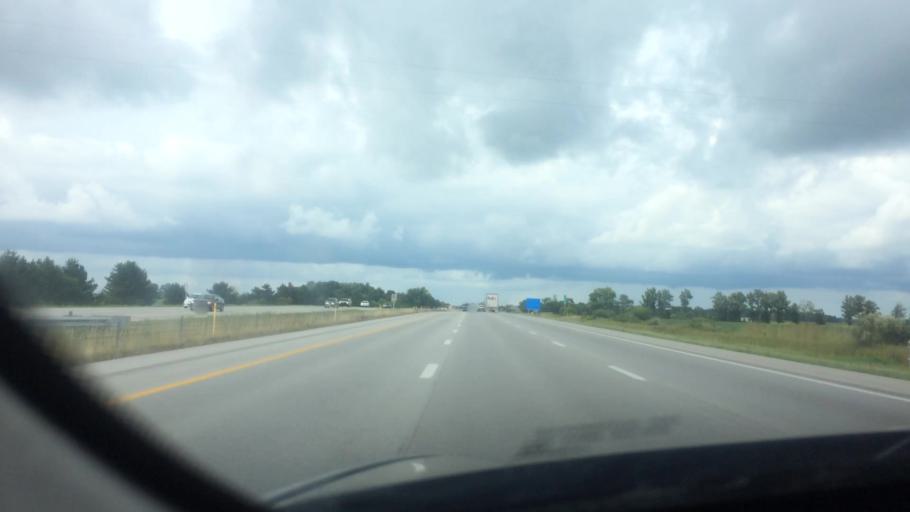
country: US
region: Ohio
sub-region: Wood County
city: Bowling Green
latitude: 41.2832
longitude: -83.6376
